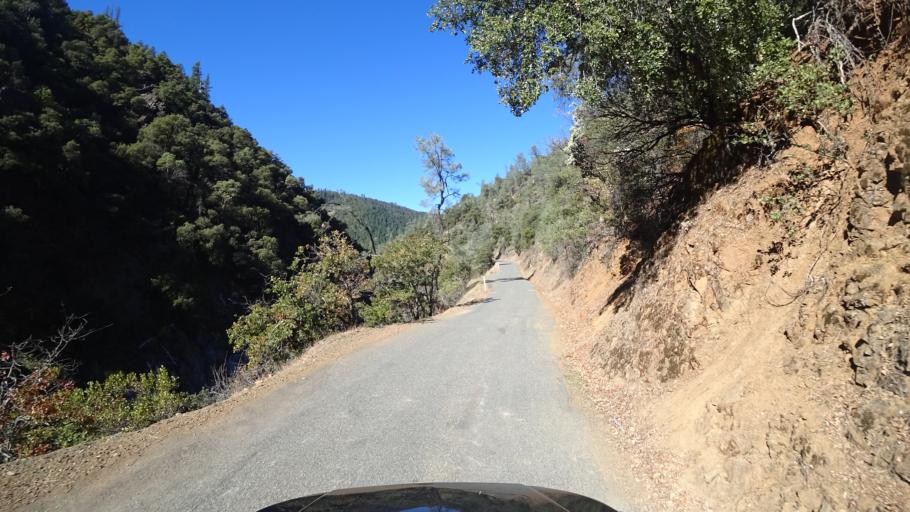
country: US
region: California
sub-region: Humboldt County
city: Willow Creek
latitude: 41.2194
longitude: -123.2405
